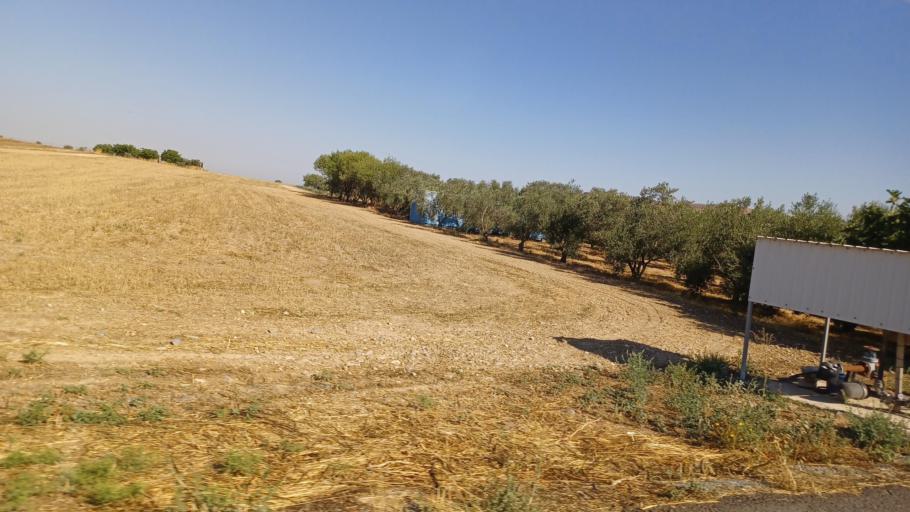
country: CY
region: Larnaka
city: Athienou
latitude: 35.0653
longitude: 33.5203
